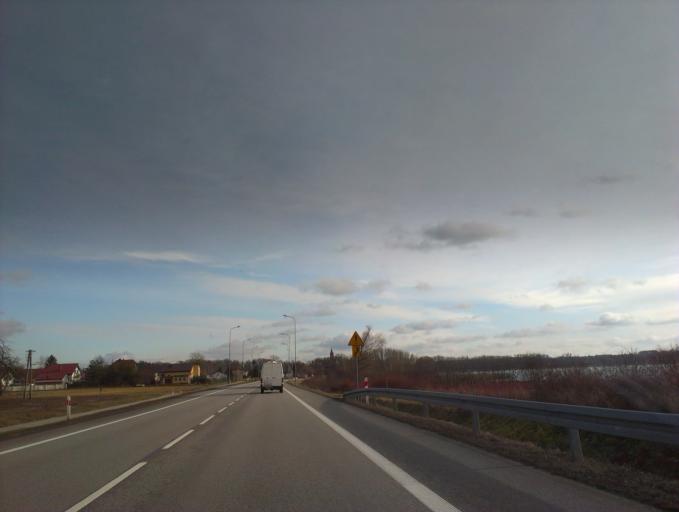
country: PL
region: Kujawsko-Pomorskie
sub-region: Powiat lipnowski
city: Kikol
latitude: 52.9156
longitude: 19.1088
